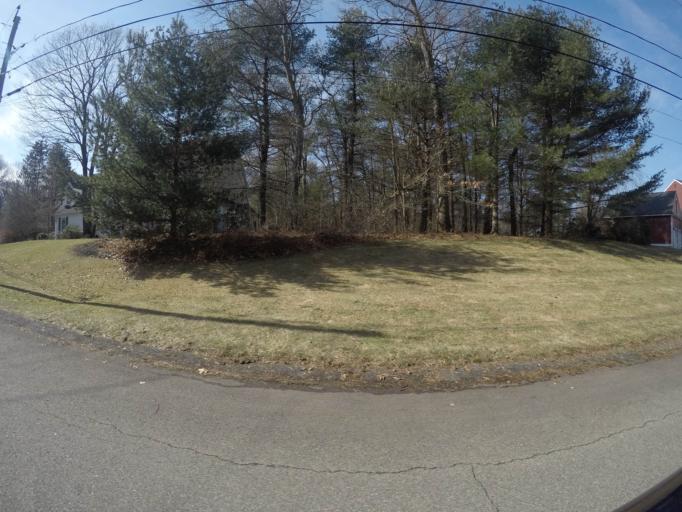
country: US
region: Massachusetts
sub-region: Bristol County
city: Easton
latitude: 42.0180
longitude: -71.1481
